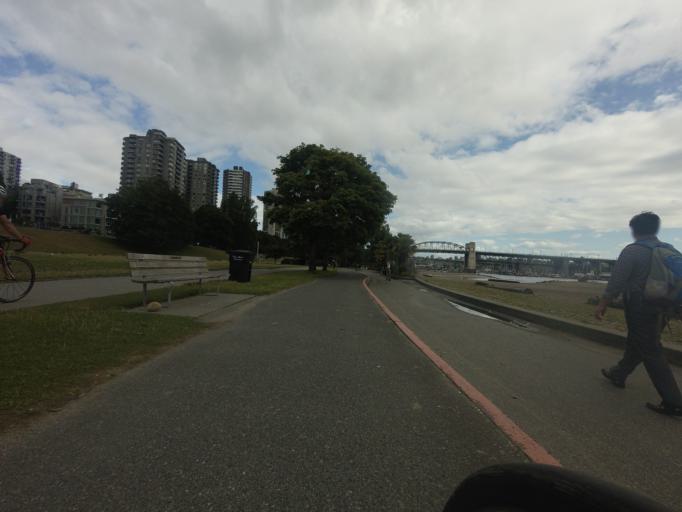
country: CA
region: British Columbia
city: West End
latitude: 49.2795
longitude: -123.1387
